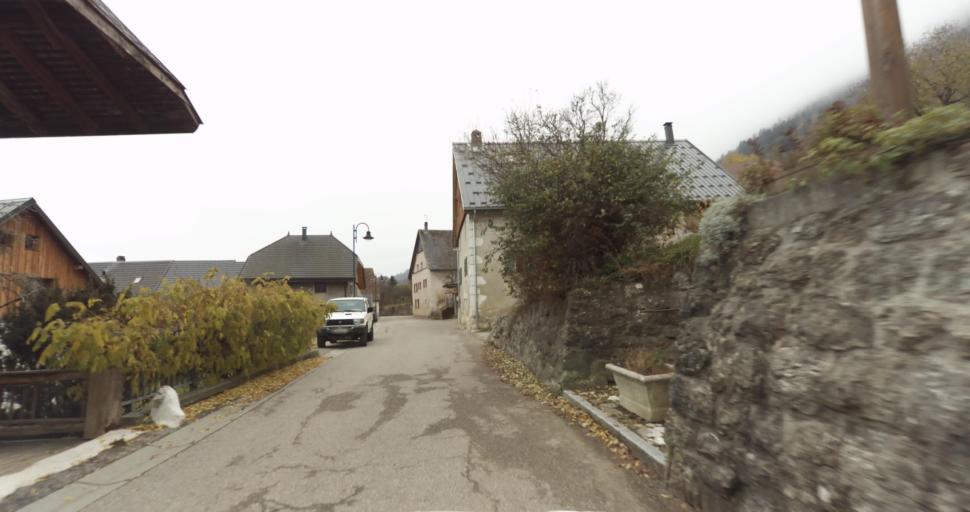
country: FR
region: Rhone-Alpes
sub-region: Departement de la Haute-Savoie
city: Doussard
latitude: 45.7950
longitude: 6.1888
